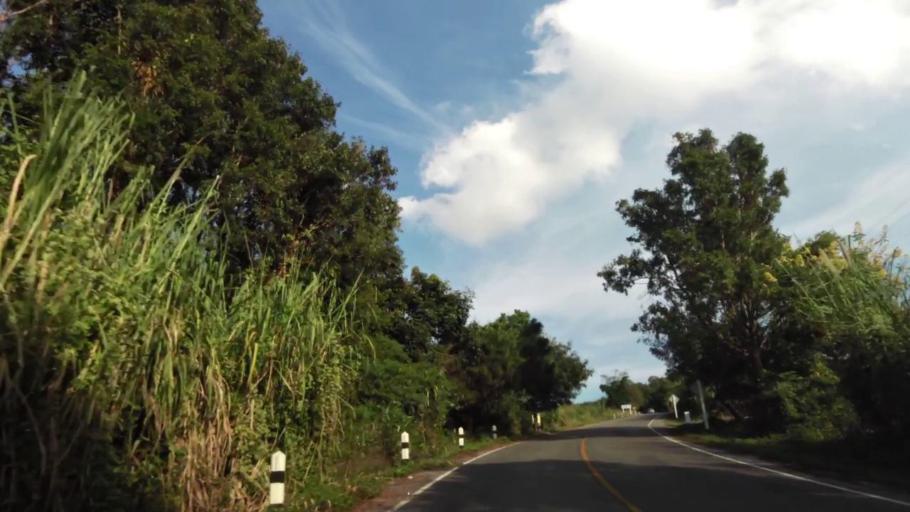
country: TH
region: Chiang Rai
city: Khun Tan
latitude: 19.8714
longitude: 100.3226
